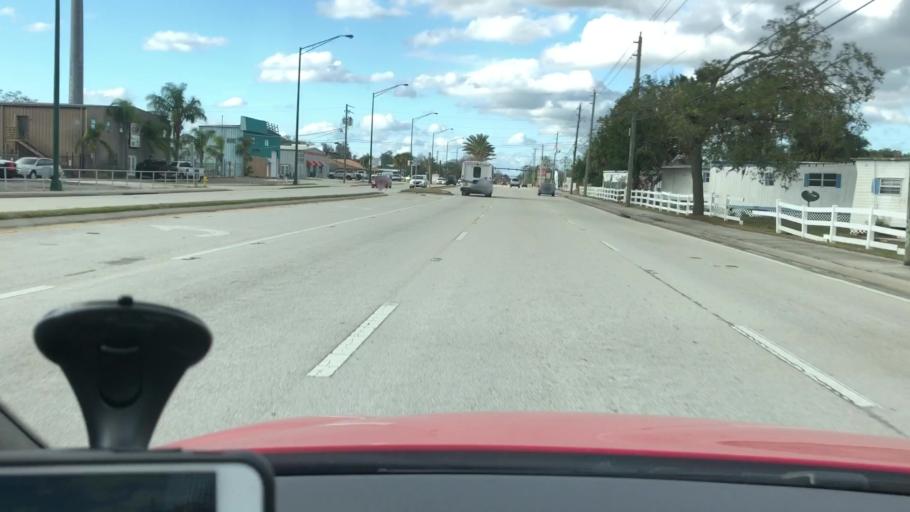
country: US
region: Florida
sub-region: Volusia County
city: Ormond Beach
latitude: 29.2575
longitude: -81.0736
